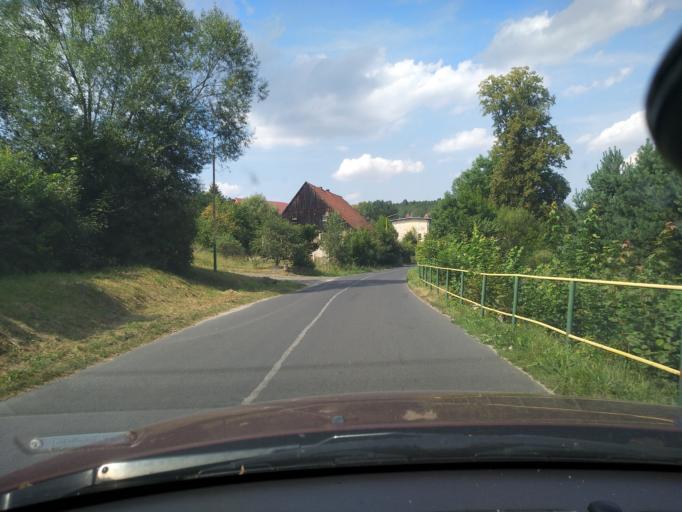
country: PL
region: Lower Silesian Voivodeship
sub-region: Powiat jeleniogorski
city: Stara Kamienica
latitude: 50.9027
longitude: 15.5694
